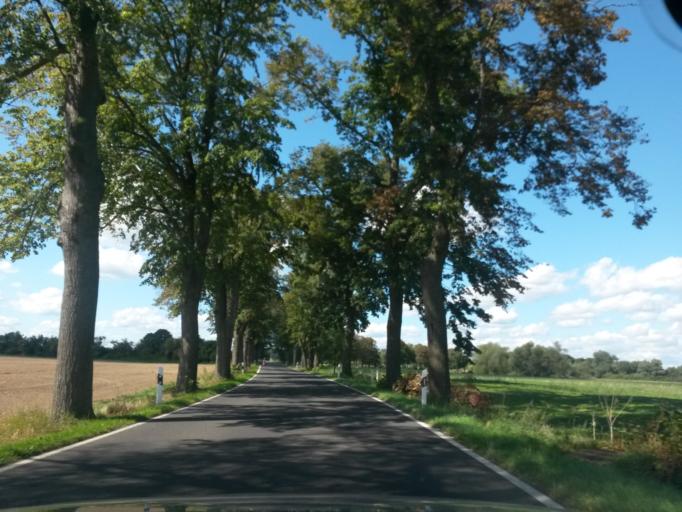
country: DE
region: Brandenburg
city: Angermunde
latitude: 53.0093
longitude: 14.0545
